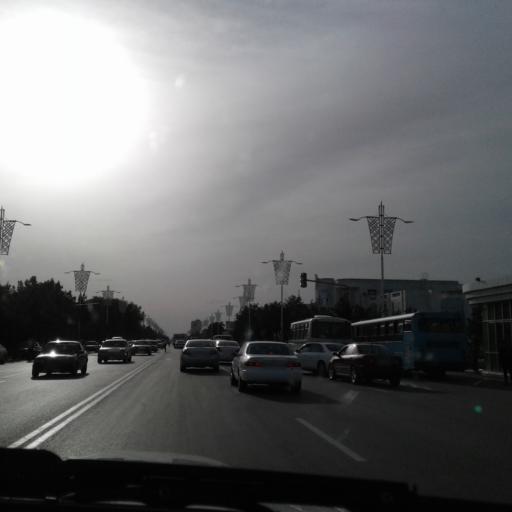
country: TM
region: Mary
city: Mary
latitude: 37.5921
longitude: 61.8447
